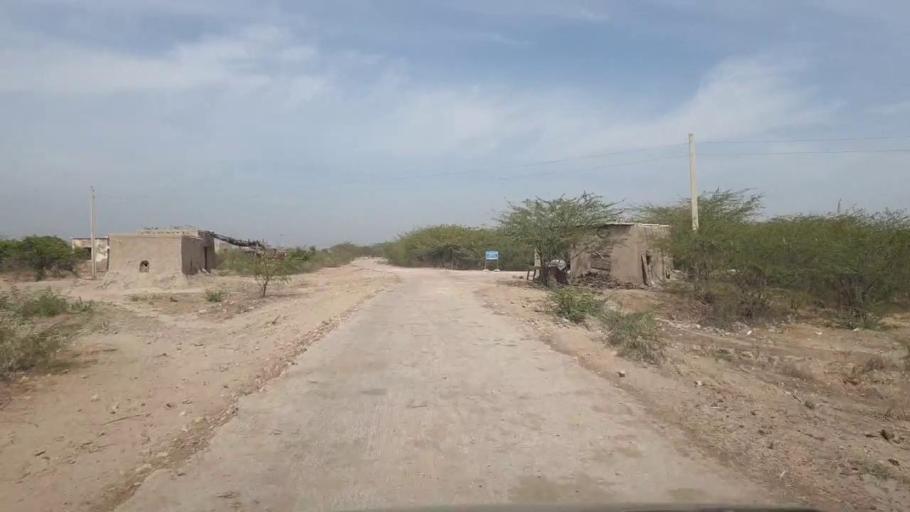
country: PK
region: Sindh
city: Kunri
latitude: 25.2359
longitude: 69.6695
